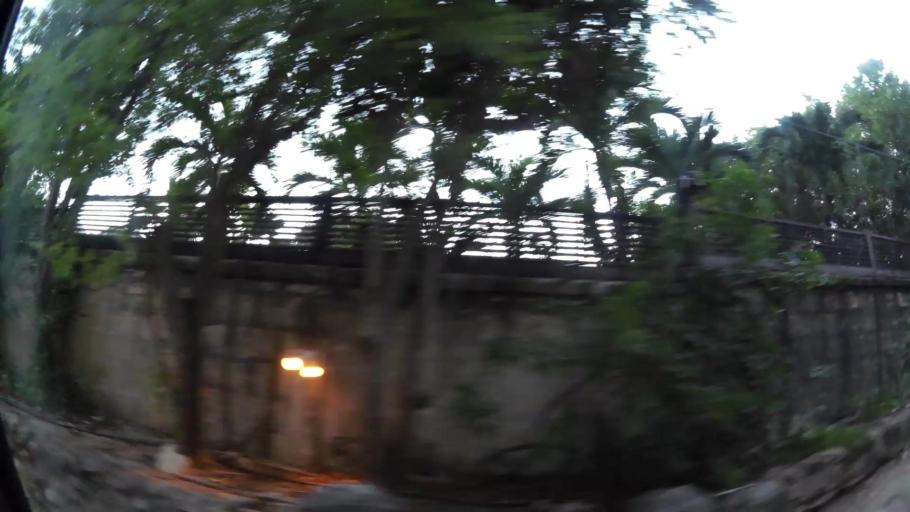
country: BB
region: Saint Philip
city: Crane
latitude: 13.1081
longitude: -59.4433
